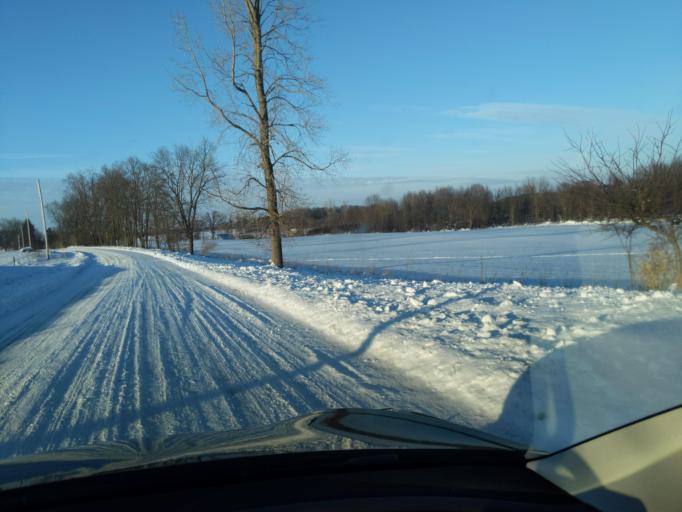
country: US
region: Michigan
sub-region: Ingham County
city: Stockbridge
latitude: 42.5010
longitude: -84.1192
